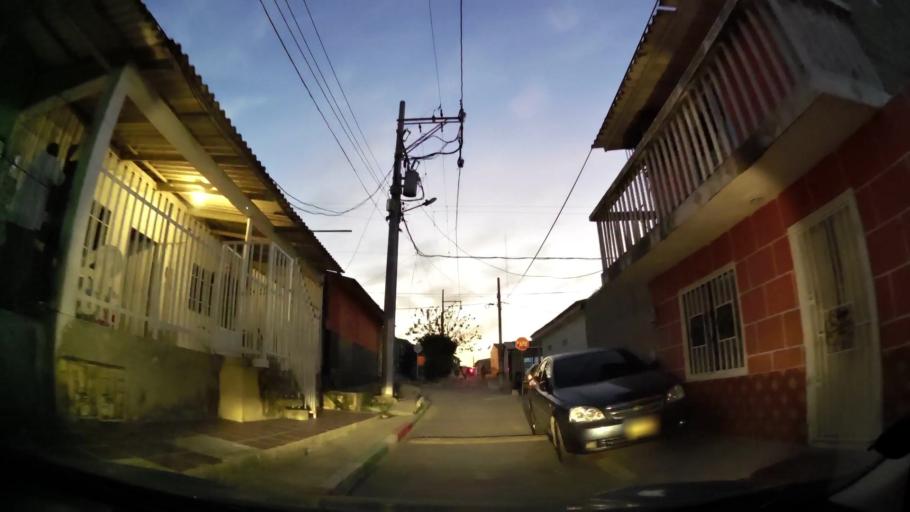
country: CO
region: Atlantico
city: Barranquilla
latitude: 10.9458
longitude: -74.8240
